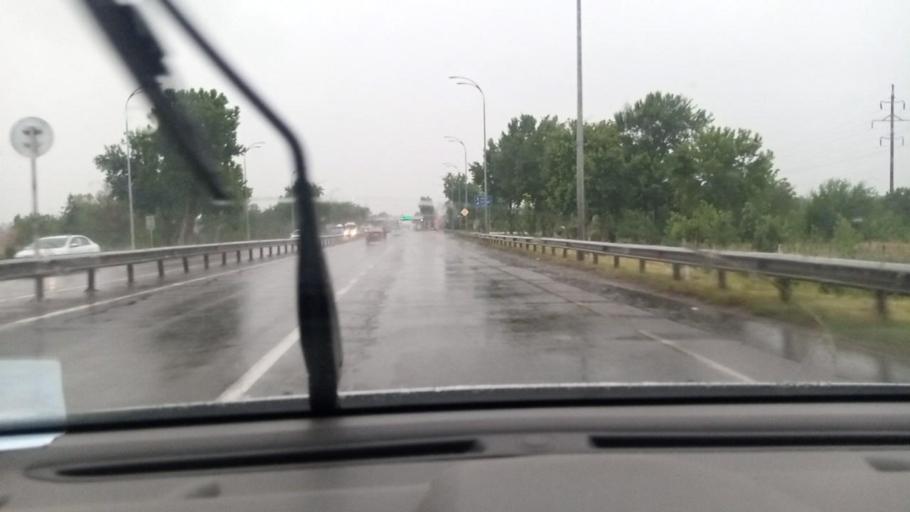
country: UZ
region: Toshkent Shahri
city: Bektemir
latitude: 41.2506
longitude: 69.3884
